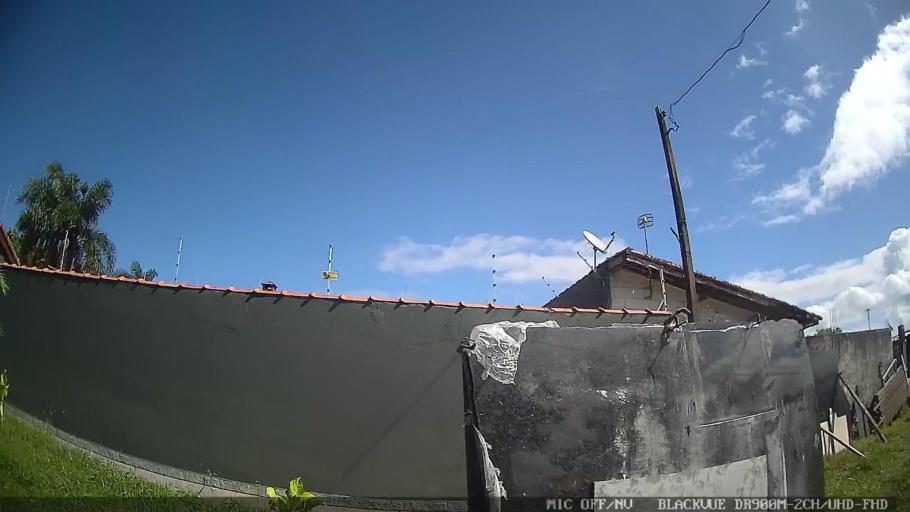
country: BR
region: Sao Paulo
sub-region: Itanhaem
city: Itanhaem
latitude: -24.2240
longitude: -46.8741
